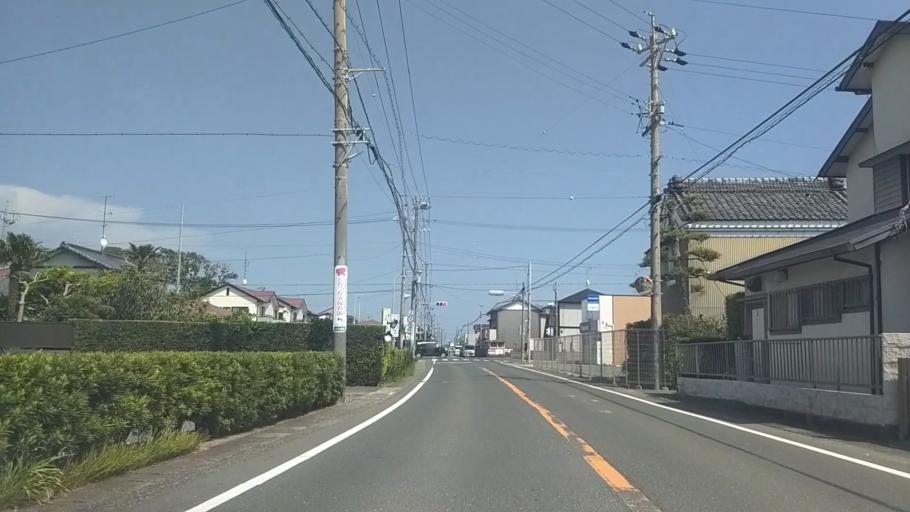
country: JP
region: Shizuoka
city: Hamamatsu
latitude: 34.6827
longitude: 137.6808
